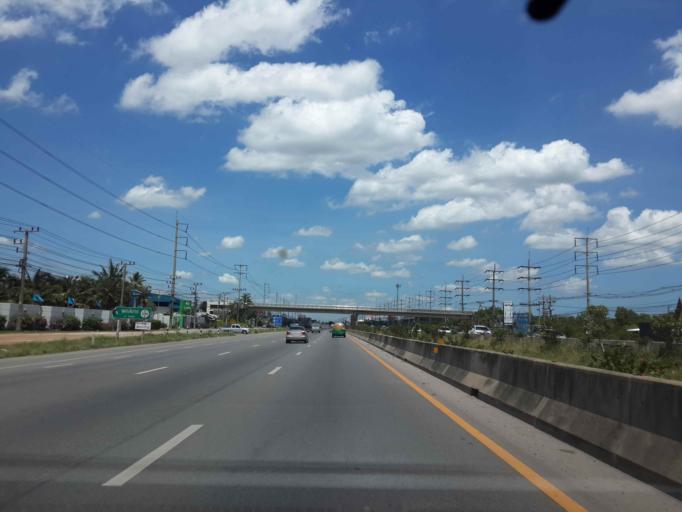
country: TH
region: Samut Sakhon
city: Ban Phaeo
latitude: 13.5180
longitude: 100.1650
